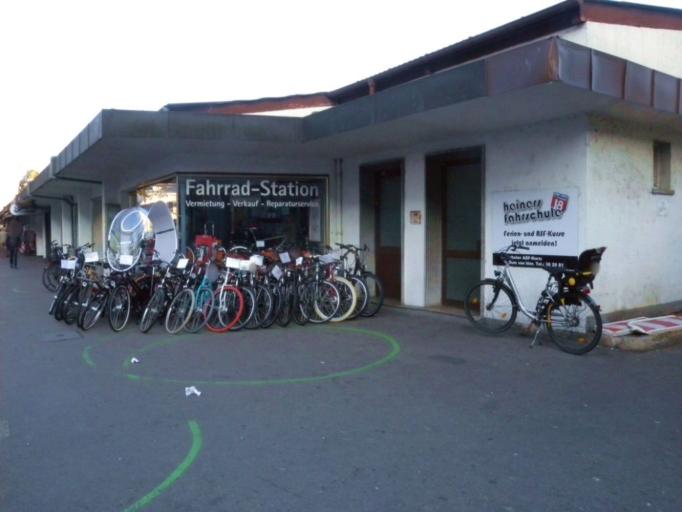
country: DE
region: Baden-Wuerttemberg
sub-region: Freiburg Region
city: Konstanz
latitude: 47.6595
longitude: 9.1772
